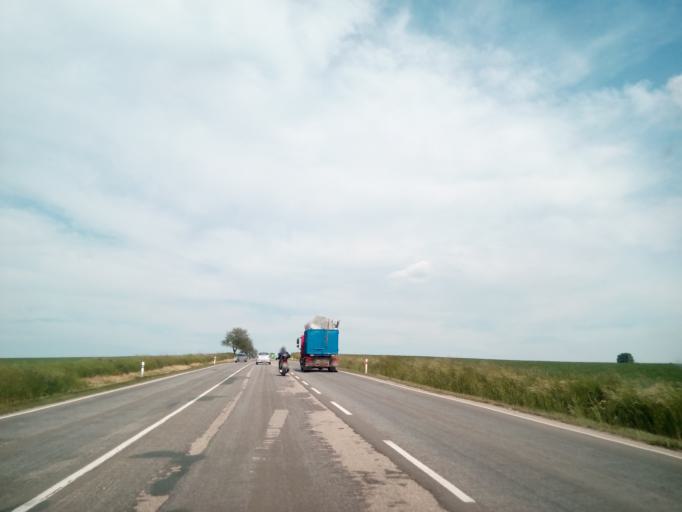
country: CZ
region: South Moravian
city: Podoli
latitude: 49.1823
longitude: 16.7304
